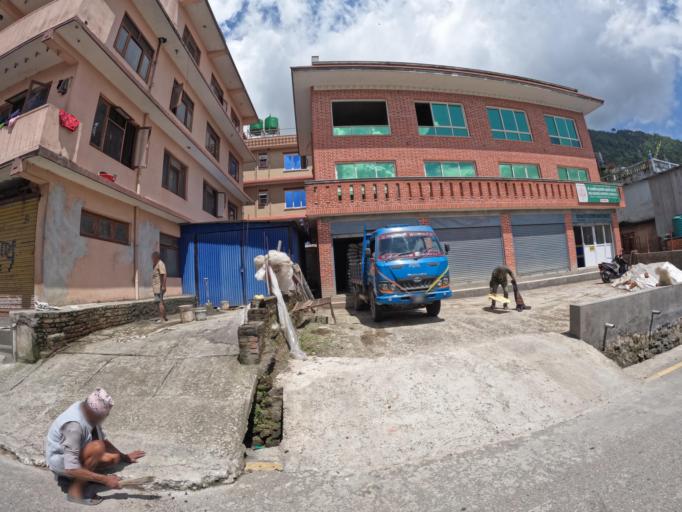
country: NP
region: Central Region
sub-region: Bagmati Zone
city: Kathmandu
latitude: 27.7920
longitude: 85.3301
